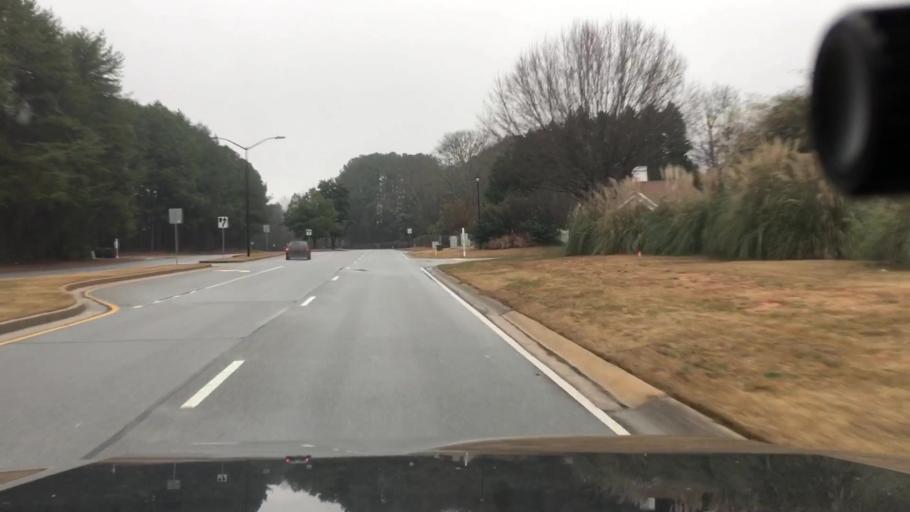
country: US
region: Georgia
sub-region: Coweta County
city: East Newnan
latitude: 33.3905
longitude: -84.7349
